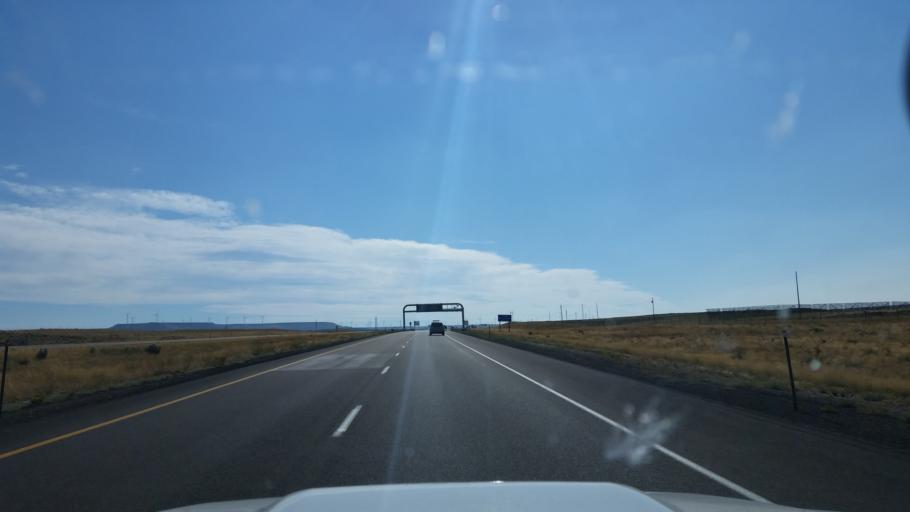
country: US
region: Wyoming
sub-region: Uinta County
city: Mountain View
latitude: 41.3364
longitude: -110.4116
